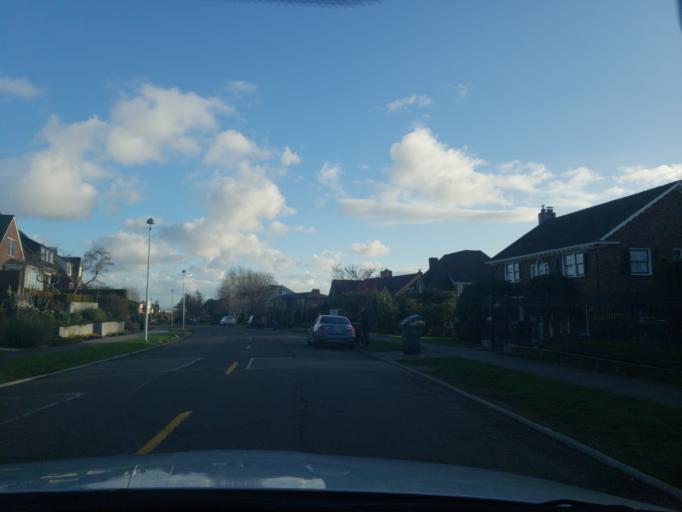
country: US
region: Washington
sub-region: King County
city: Seattle
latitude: 47.6402
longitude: -122.4094
